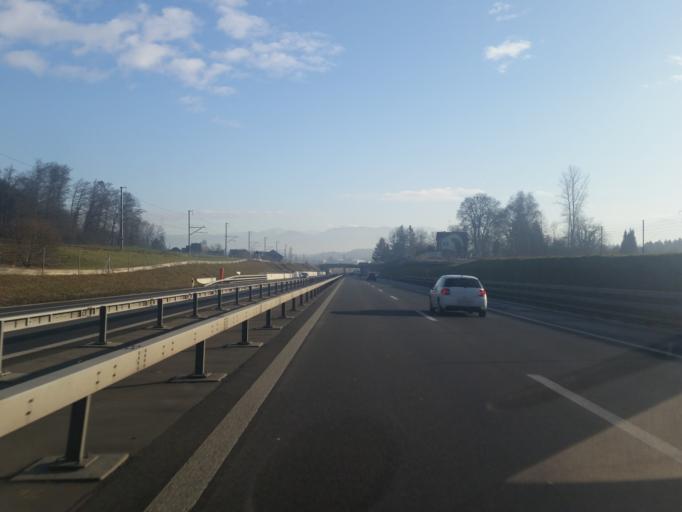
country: CH
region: Zurich
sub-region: Bezirk Affoltern
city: Obfelden / Toussen
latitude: 47.2562
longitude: 8.4446
